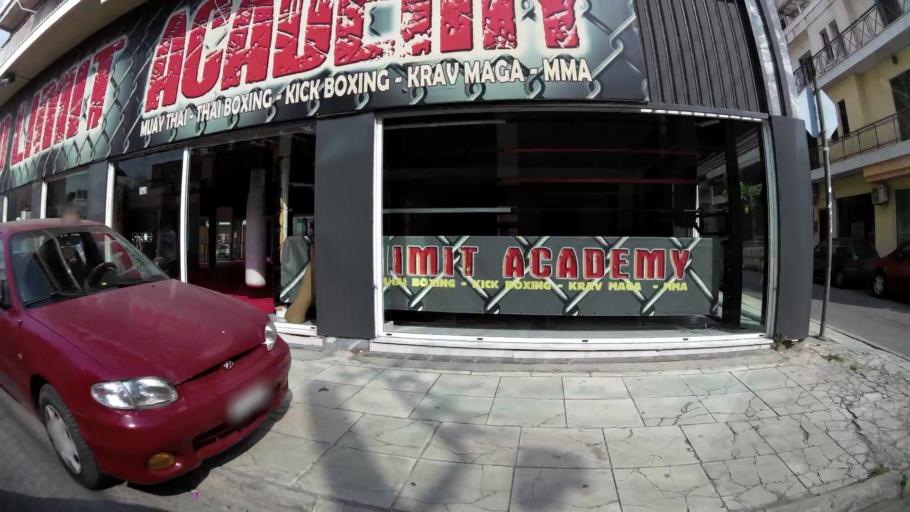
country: GR
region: Attica
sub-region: Nomarchia Athinas
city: Peristeri
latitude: 38.0165
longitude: 23.6813
